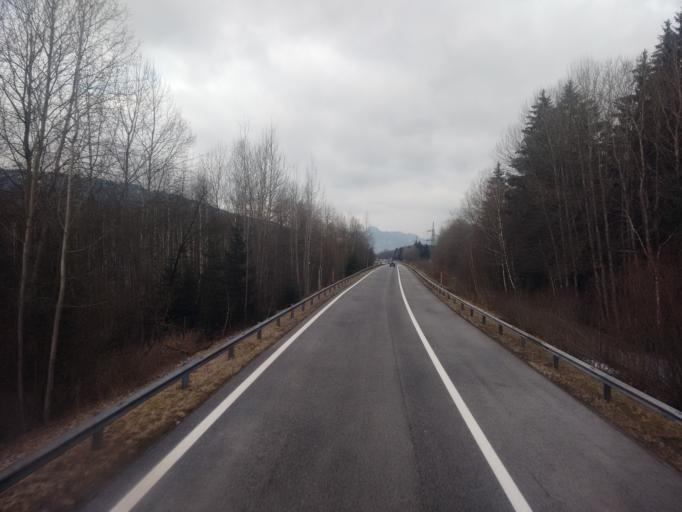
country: AT
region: Styria
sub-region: Politischer Bezirk Liezen
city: Selzthal
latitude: 47.5572
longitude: 14.2976
